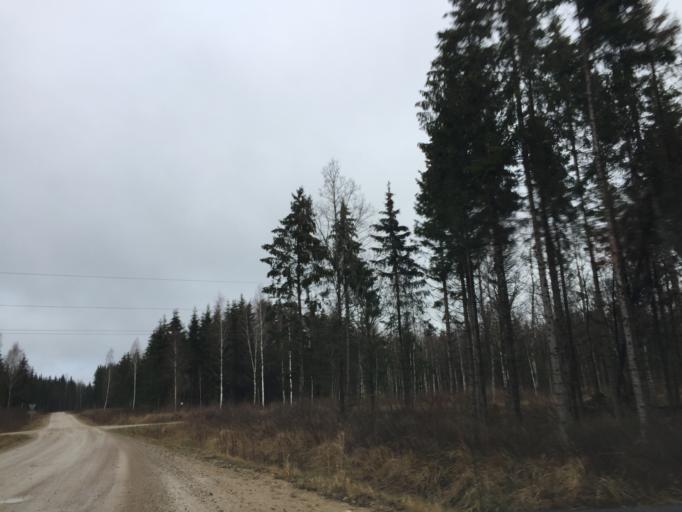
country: LV
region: Saldus Rajons
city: Saldus
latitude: 56.6705
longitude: 22.4029
